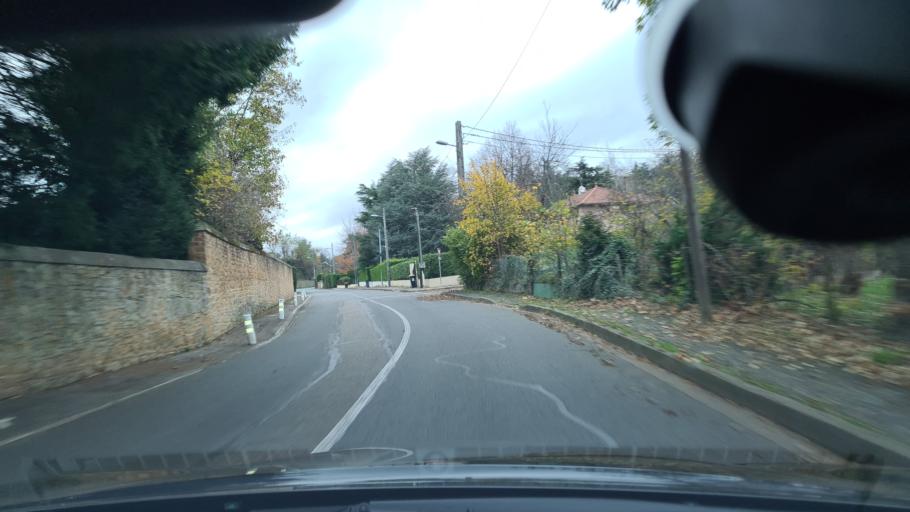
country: FR
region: Rhone-Alpes
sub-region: Departement du Rhone
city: Fontaines-sur-Saone
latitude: 45.8231
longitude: 4.8104
